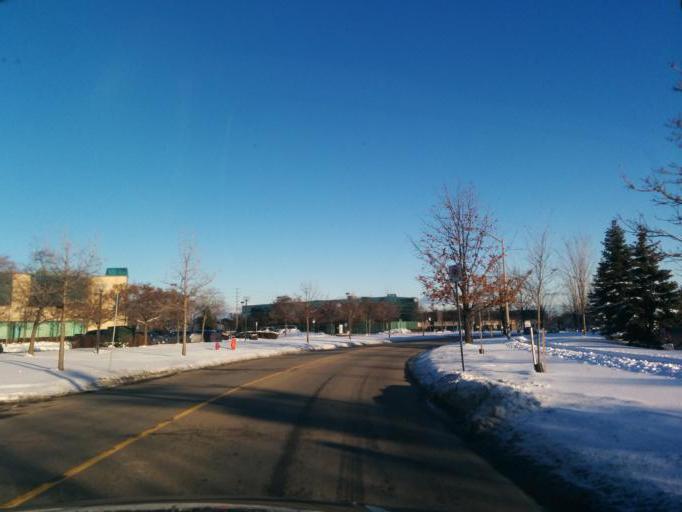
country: CA
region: Ontario
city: Mississauga
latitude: 43.5198
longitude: -79.6804
